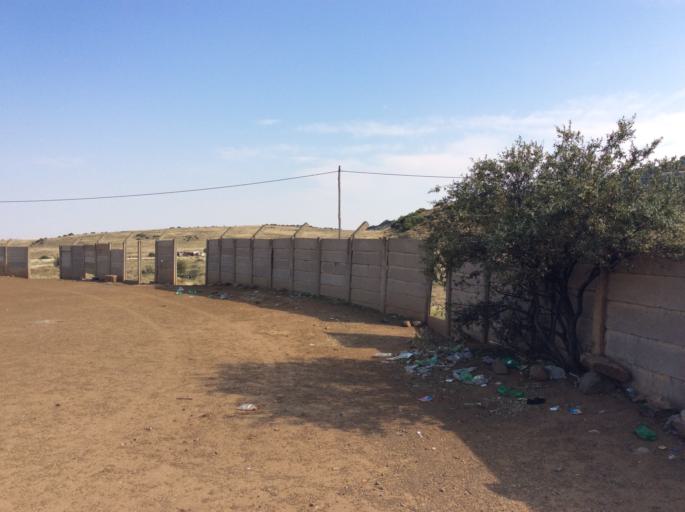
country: LS
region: Mafeteng
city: Mafeteng
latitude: -29.7146
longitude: 27.0320
